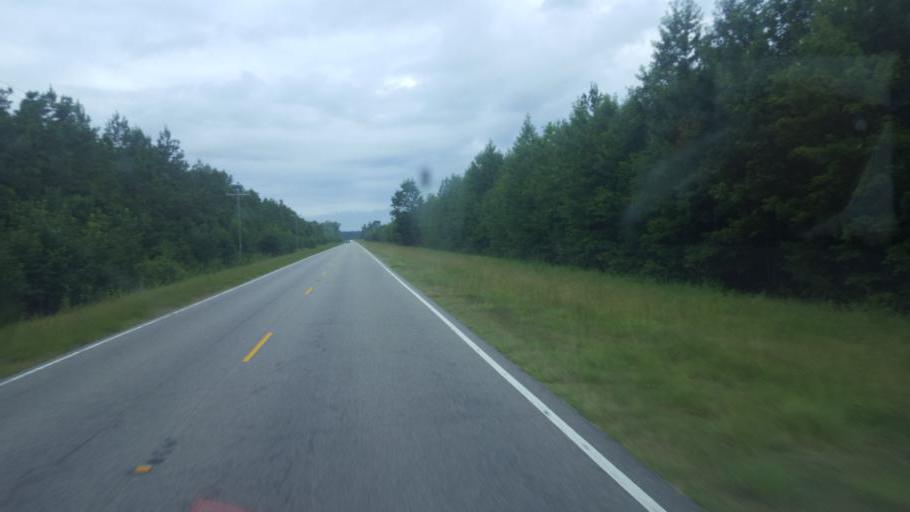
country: US
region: North Carolina
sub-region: Tyrrell County
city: Columbia
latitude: 35.9328
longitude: -76.1703
